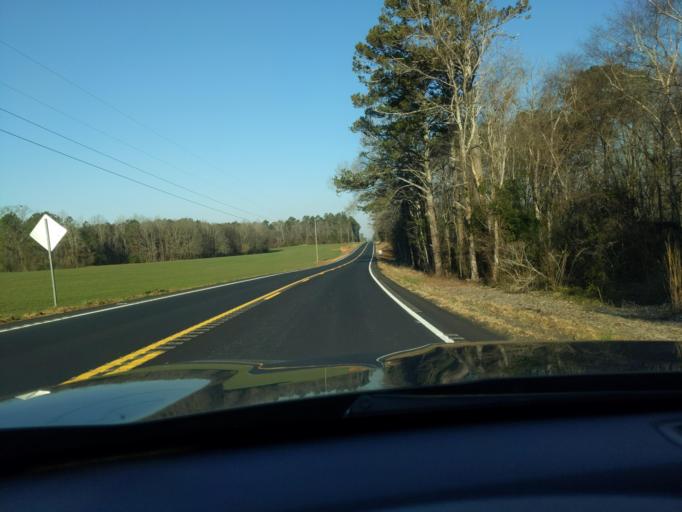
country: US
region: South Carolina
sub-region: Newberry County
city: Newberry
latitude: 34.1970
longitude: -81.7975
